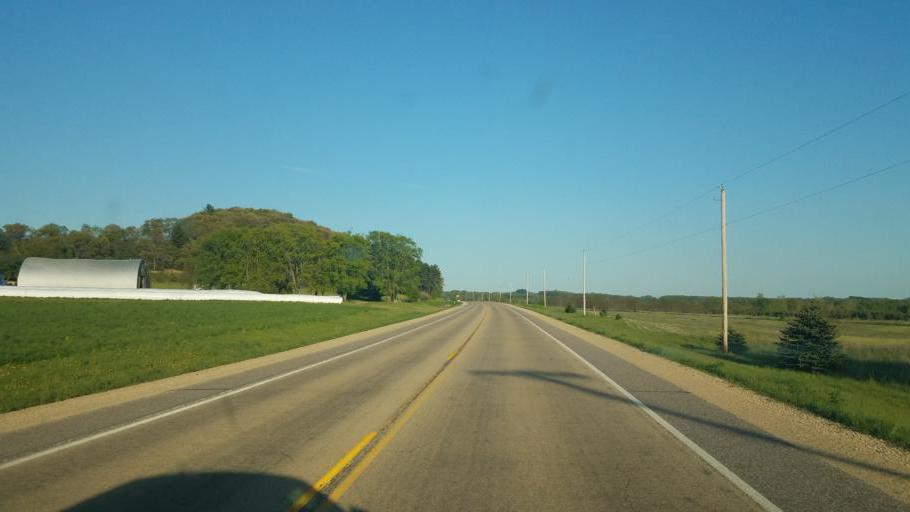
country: US
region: Wisconsin
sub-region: Juneau County
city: Elroy
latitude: 43.6226
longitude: -90.1620
